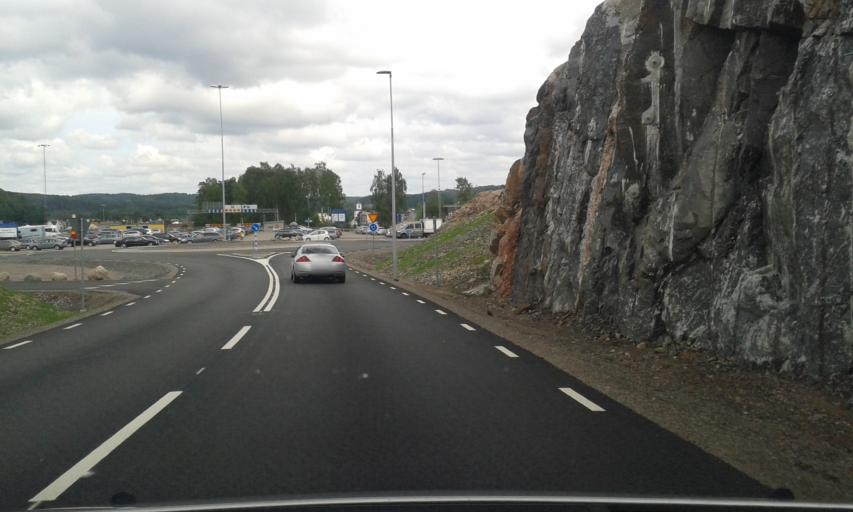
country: SE
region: Halland
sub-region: Falkenbergs Kommun
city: Falkenberg
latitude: 57.1361
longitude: 12.7057
